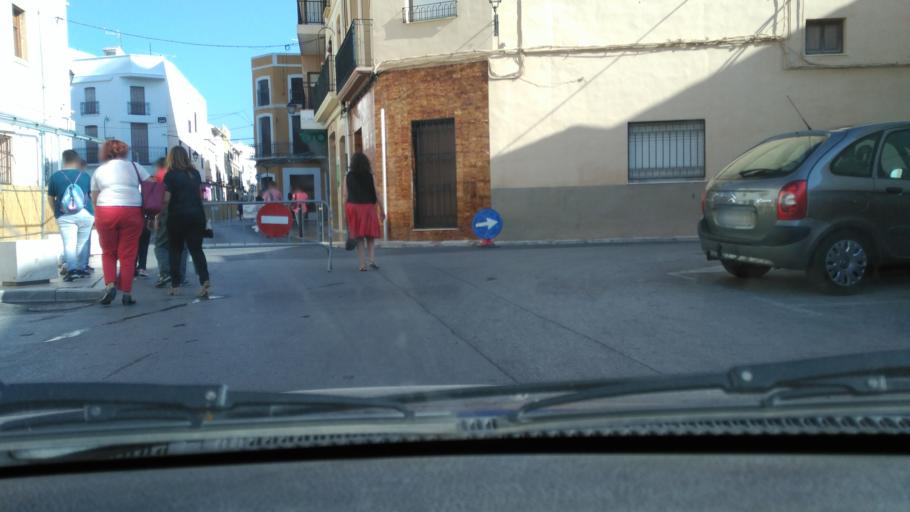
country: ES
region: Valencia
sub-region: Provincia de Alicante
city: Gata de Gorgos
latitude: 38.7730
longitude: 0.0842
